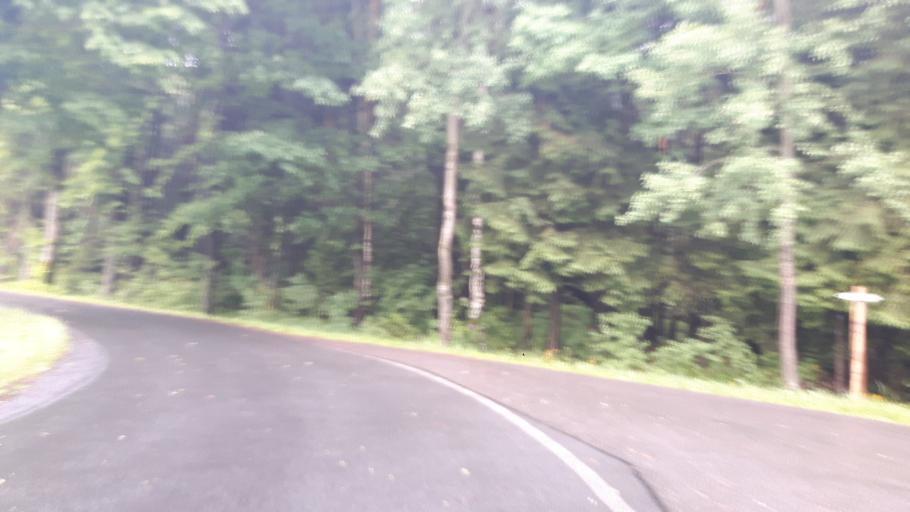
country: DE
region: Thuringia
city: Bockstadt
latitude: 50.4066
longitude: 10.8949
